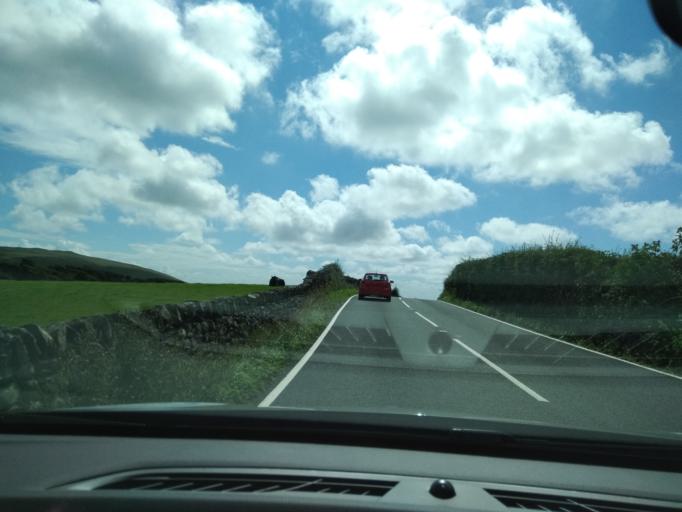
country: GB
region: England
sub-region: Cumbria
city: Millom
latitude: 54.2390
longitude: -3.3211
